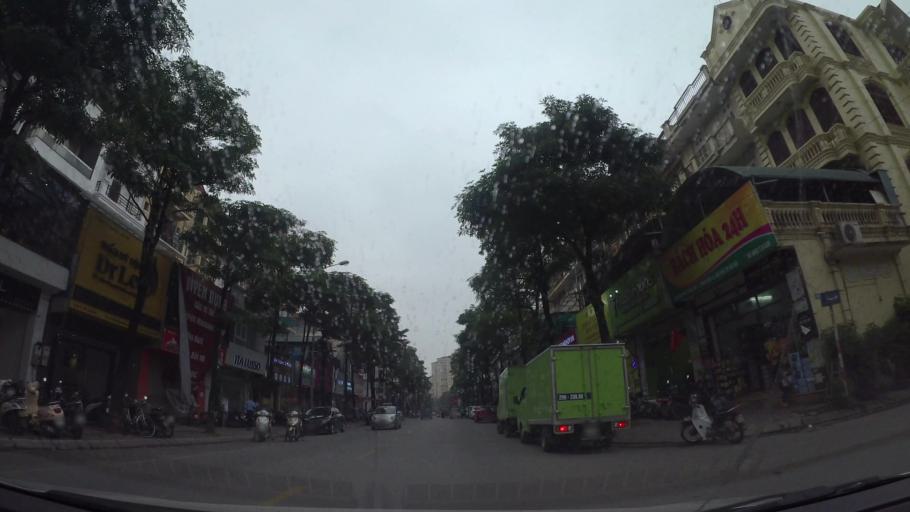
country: VN
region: Ha Noi
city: Cau Giay
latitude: 21.0146
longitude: 105.8018
